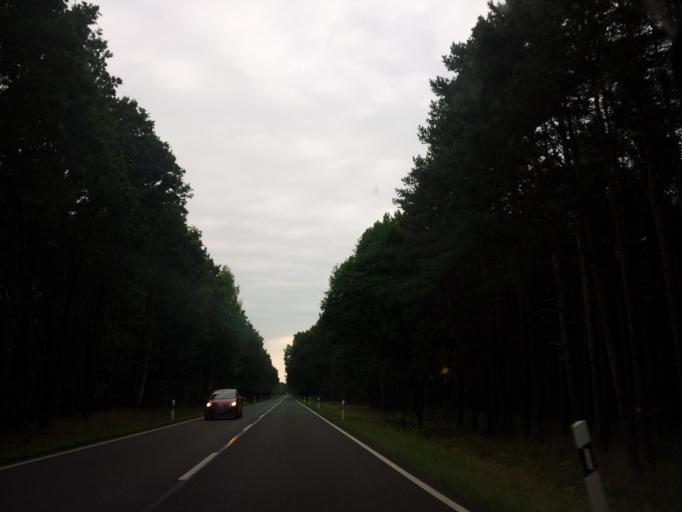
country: DE
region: Brandenburg
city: Treuenbrietzen
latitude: 52.0507
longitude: 12.9119
